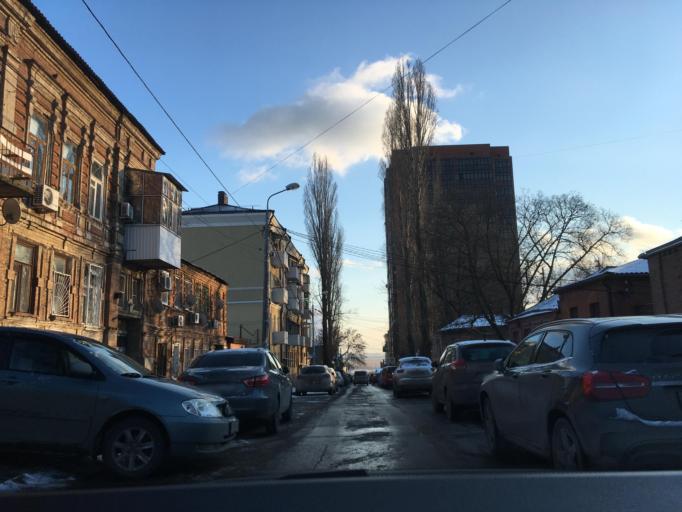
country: RU
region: Rostov
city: Rostov-na-Donu
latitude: 47.2248
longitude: 39.7371
